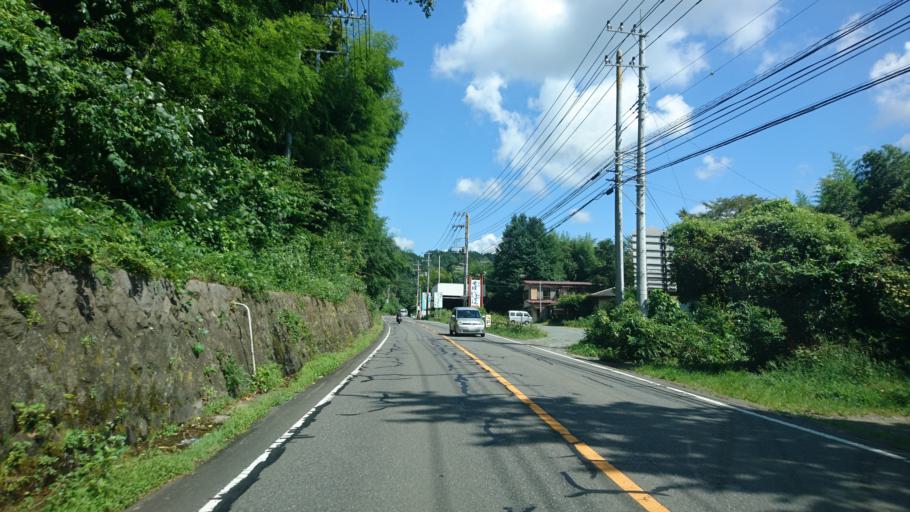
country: JP
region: Gunma
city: Omamacho-omama
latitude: 36.4758
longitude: 139.2572
